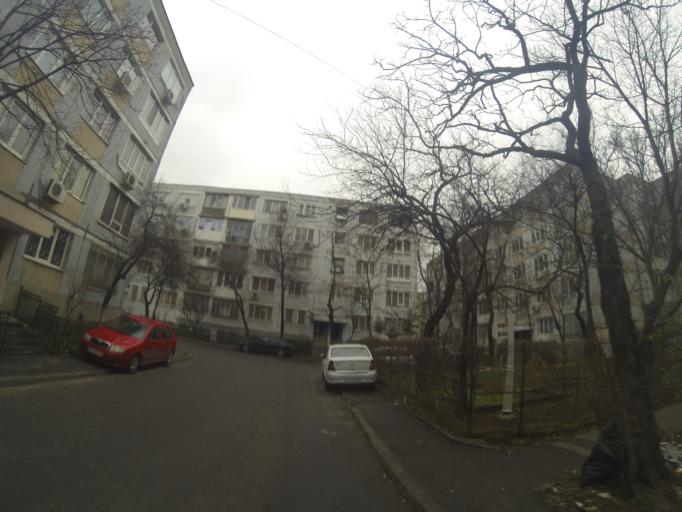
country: RO
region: Bucuresti
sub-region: Municipiul Bucuresti
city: Bucuresti
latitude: 44.4081
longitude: 26.0722
